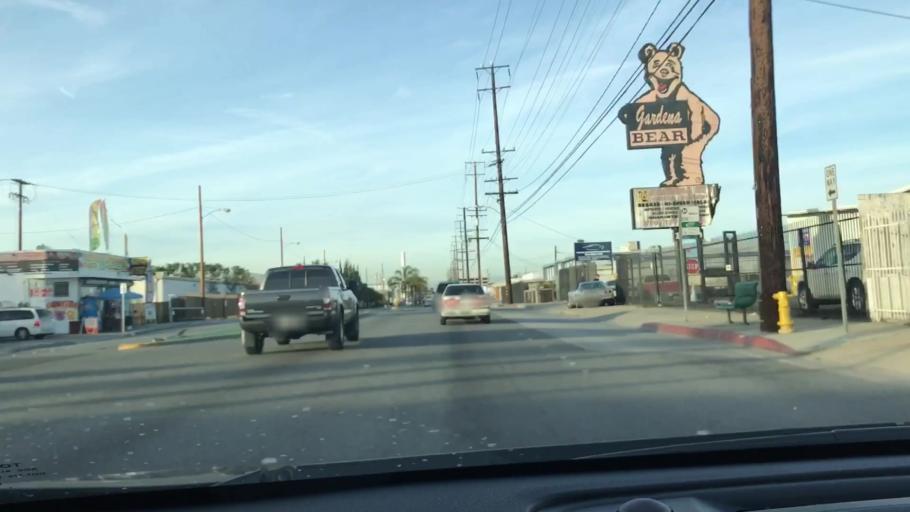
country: US
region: California
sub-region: Los Angeles County
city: Alondra Park
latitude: 33.9123
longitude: -118.3264
